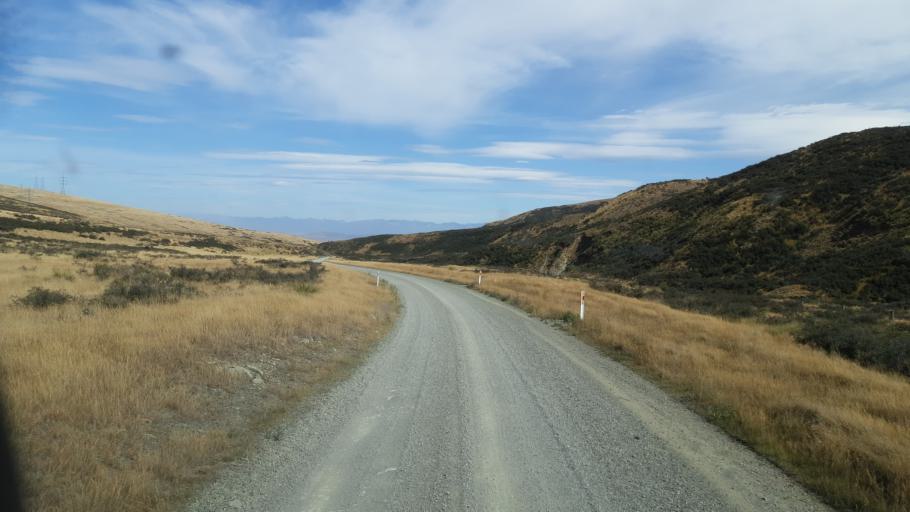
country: NZ
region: Canterbury
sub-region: Timaru District
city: Pleasant Point
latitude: -44.1942
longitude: 170.5934
